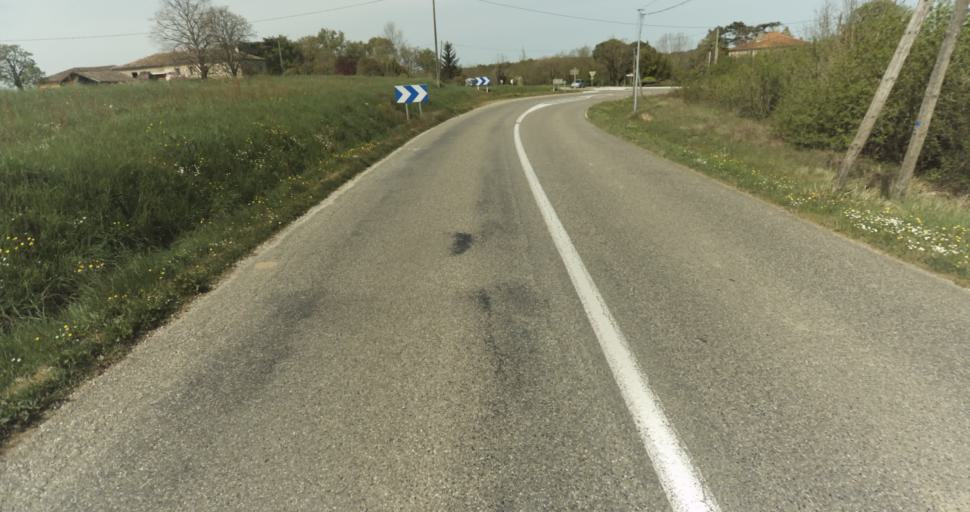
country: FR
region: Midi-Pyrenees
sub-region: Departement du Tarn-et-Garonne
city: Moissac
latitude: 44.1676
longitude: 1.0872
